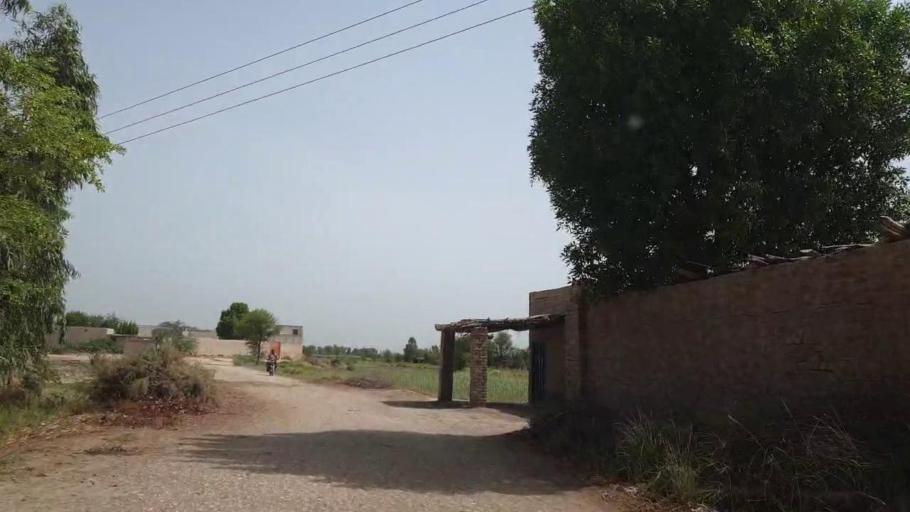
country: PK
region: Sindh
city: Sakrand
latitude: 26.1231
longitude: 68.3698
